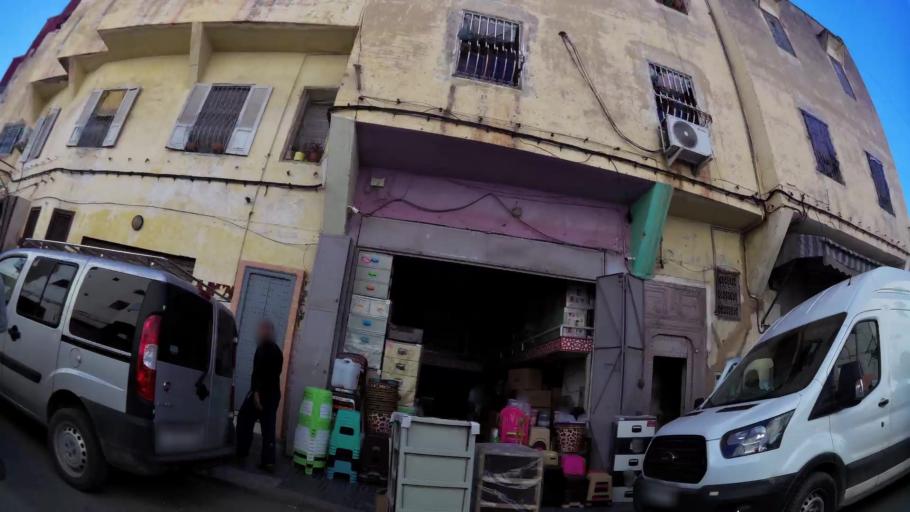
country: MA
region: Fes-Boulemane
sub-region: Fes
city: Fes
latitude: 34.0632
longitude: -4.9644
